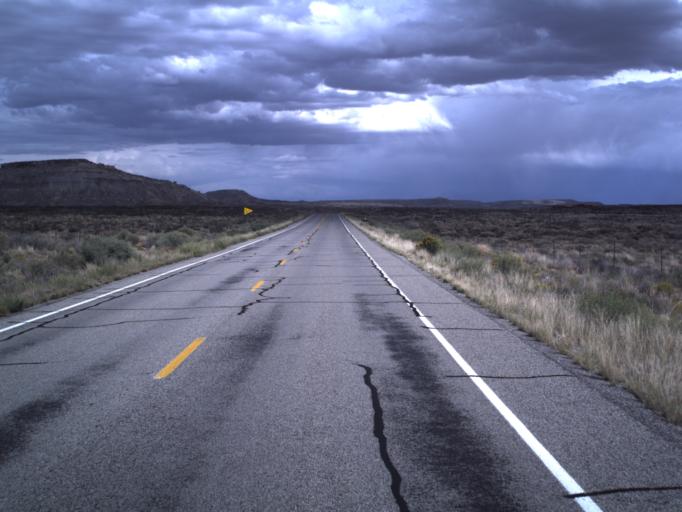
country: US
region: Utah
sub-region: San Juan County
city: Blanding
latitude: 37.2975
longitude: -109.4745
